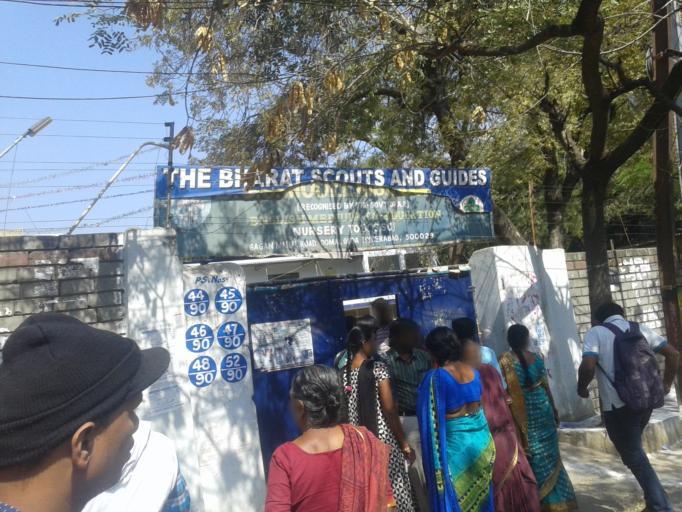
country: IN
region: Telangana
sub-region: Hyderabad
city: Hyderabad
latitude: 17.4074
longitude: 78.4808
